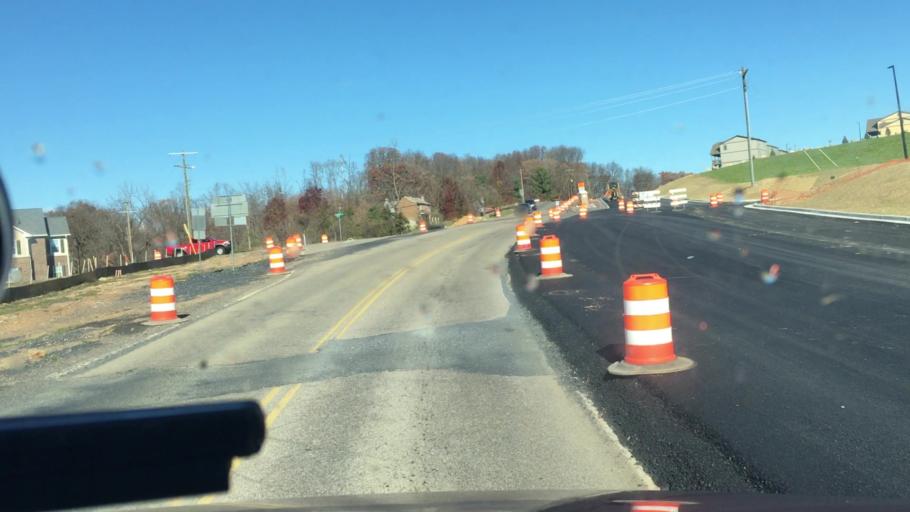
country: US
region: Virginia
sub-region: Rockingham County
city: Massanetta Springs
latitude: 38.4107
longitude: -78.8564
